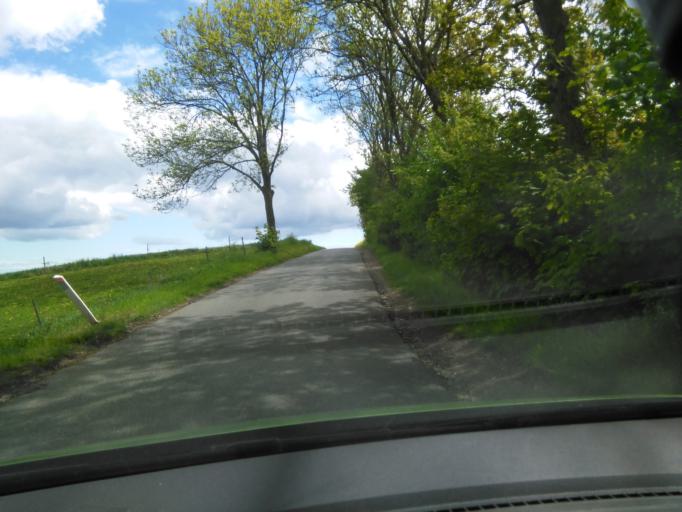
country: DK
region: Central Jutland
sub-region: Arhus Kommune
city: Tranbjerg
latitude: 56.0626
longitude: 10.1095
